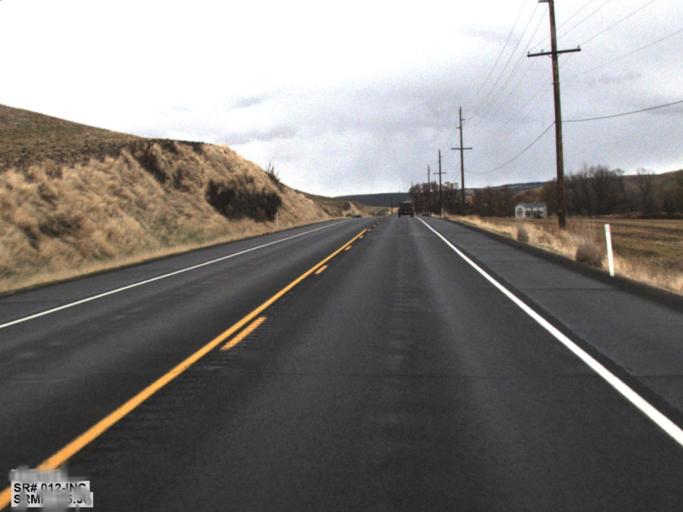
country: US
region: Washington
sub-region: Walla Walla County
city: Walla Walla East
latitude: 46.1243
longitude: -118.2026
